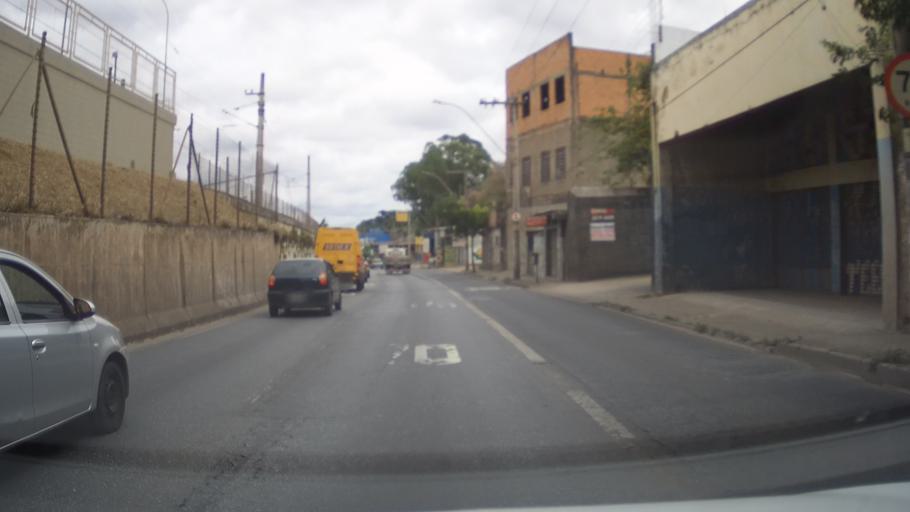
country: BR
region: Minas Gerais
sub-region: Belo Horizonte
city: Belo Horizonte
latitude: -19.8333
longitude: -43.9403
